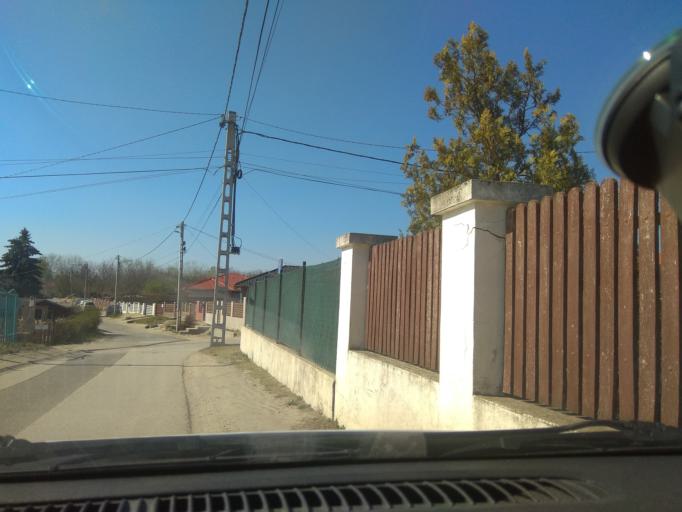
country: HU
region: Pest
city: Szigethalom
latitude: 47.3220
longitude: 19.0204
